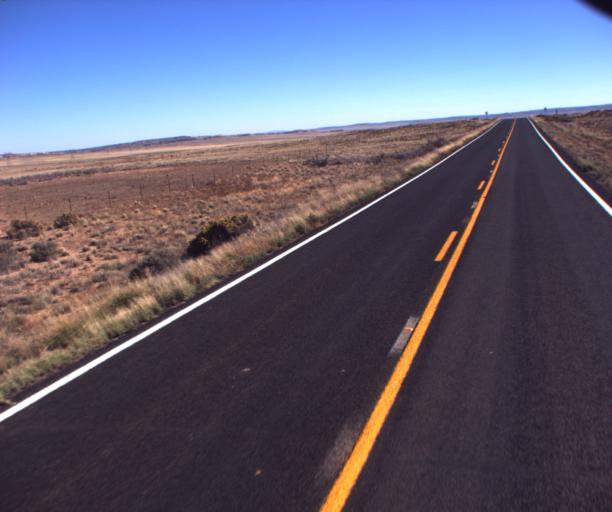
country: US
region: Arizona
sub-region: Coconino County
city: Tuba City
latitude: 35.9706
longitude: -110.8252
